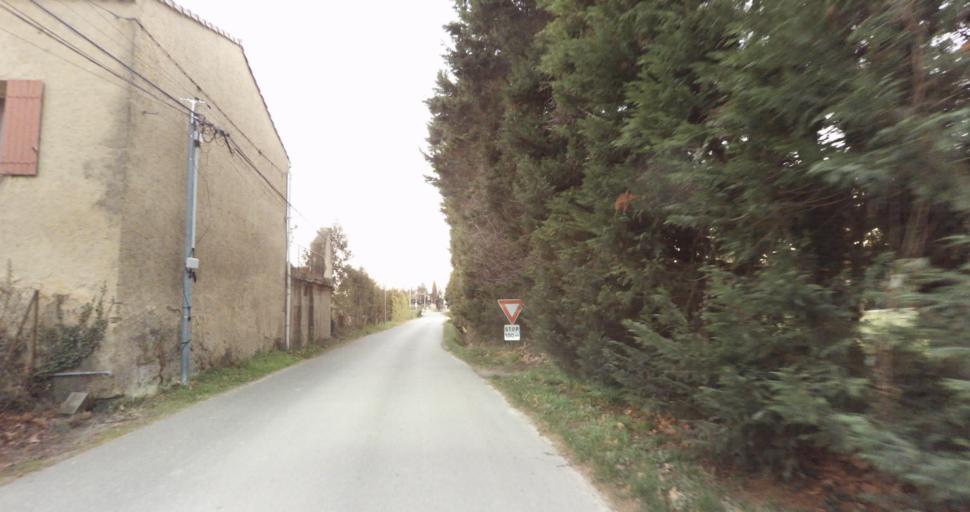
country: FR
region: Provence-Alpes-Cote d'Azur
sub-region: Departement des Bouches-du-Rhone
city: Barbentane
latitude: 43.9086
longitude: 4.7762
